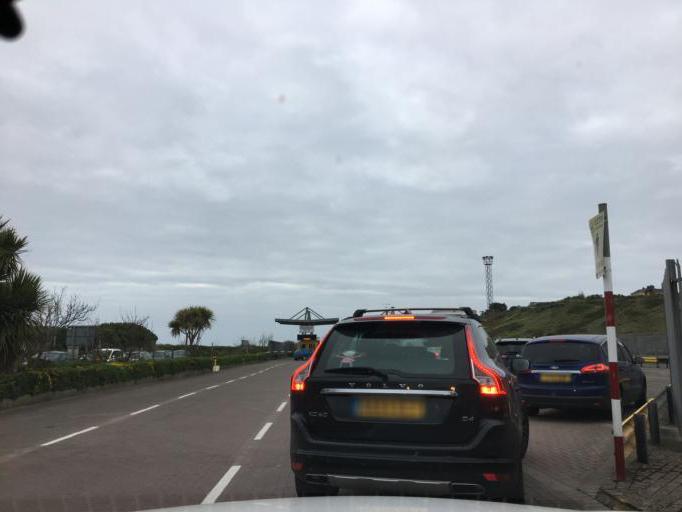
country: IE
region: Leinster
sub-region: Loch Garman
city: Ballygerry
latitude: 52.2520
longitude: -6.3349
